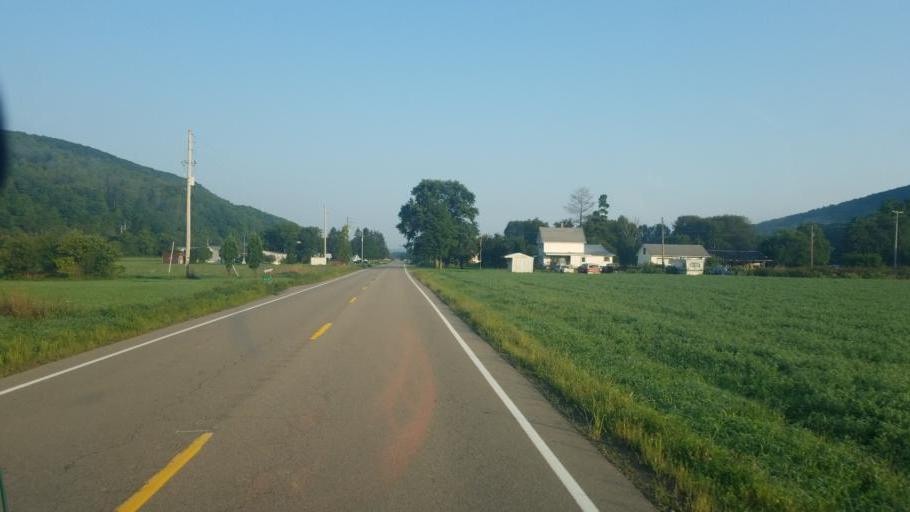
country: US
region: Pennsylvania
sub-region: Tioga County
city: Westfield
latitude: 41.9703
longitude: -77.4555
